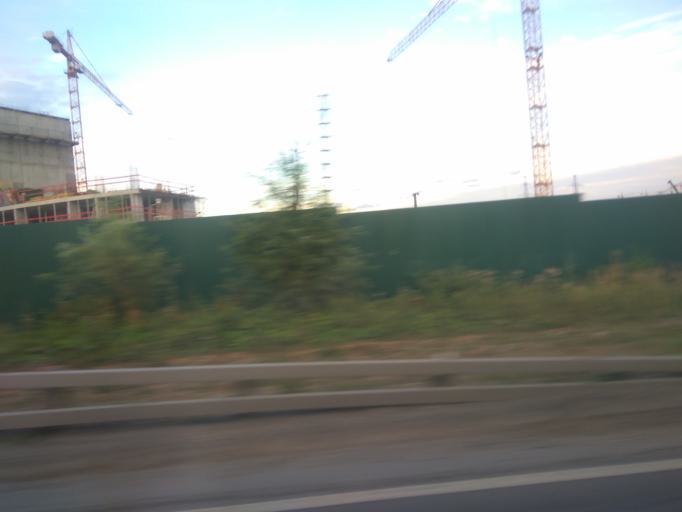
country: RU
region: Moscow
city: Solntsevo
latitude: 55.6323
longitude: 37.4113
